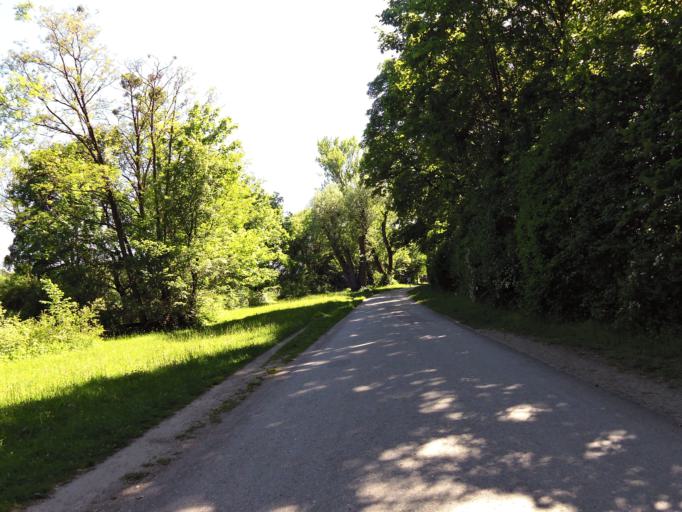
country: DE
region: Bavaria
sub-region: Upper Bavaria
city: Bogenhausen
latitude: 48.1675
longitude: 11.6142
